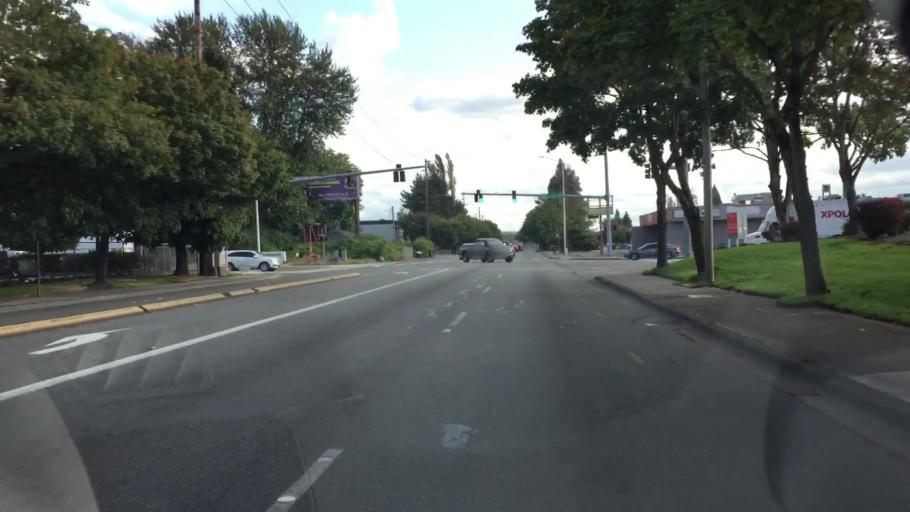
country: US
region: Washington
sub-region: King County
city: Kent
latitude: 47.4268
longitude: -122.2281
